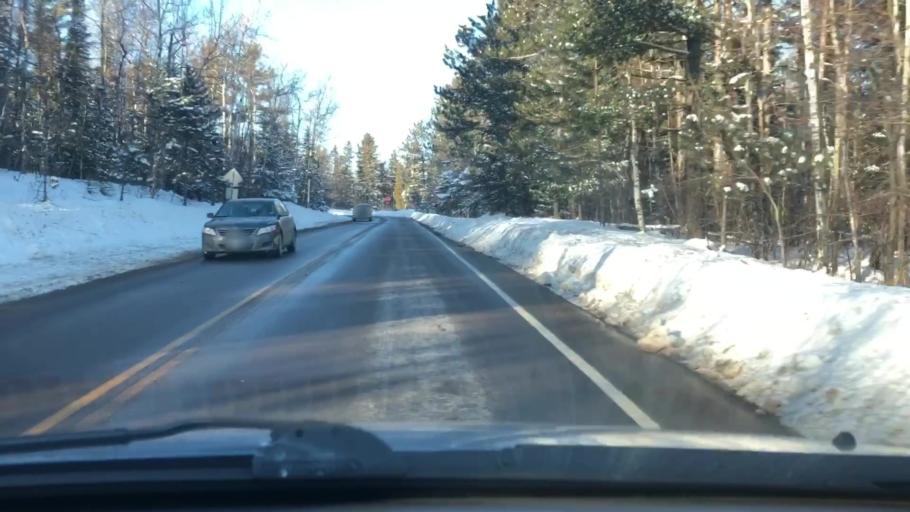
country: US
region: Minnesota
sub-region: Saint Louis County
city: Duluth
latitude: 46.8207
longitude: -92.0695
